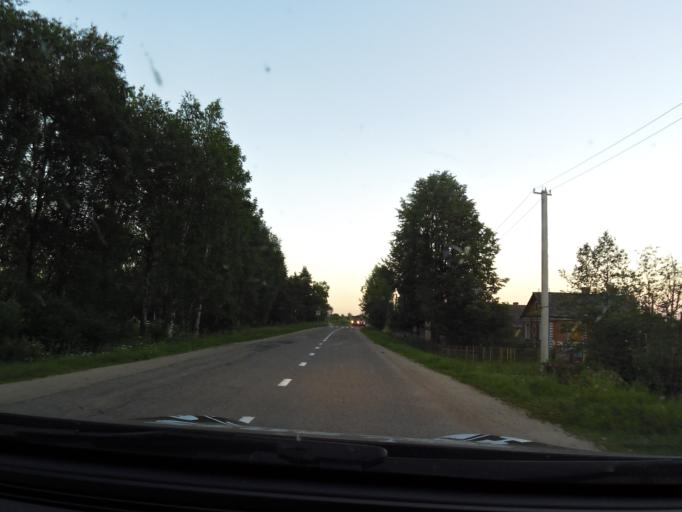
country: RU
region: Jaroslavl
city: Lyubim
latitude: 58.3230
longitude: 41.0144
